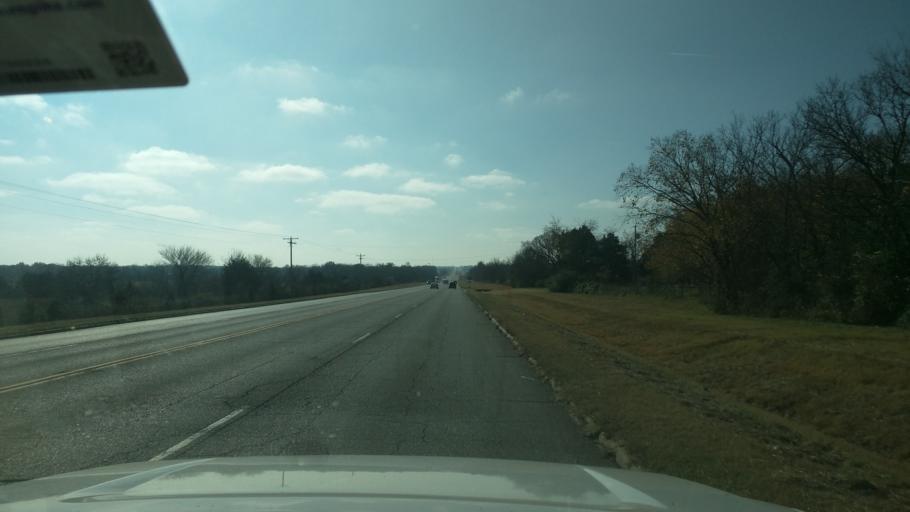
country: US
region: Oklahoma
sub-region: Washington County
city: Bartlesville
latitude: 36.6788
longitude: -95.9353
